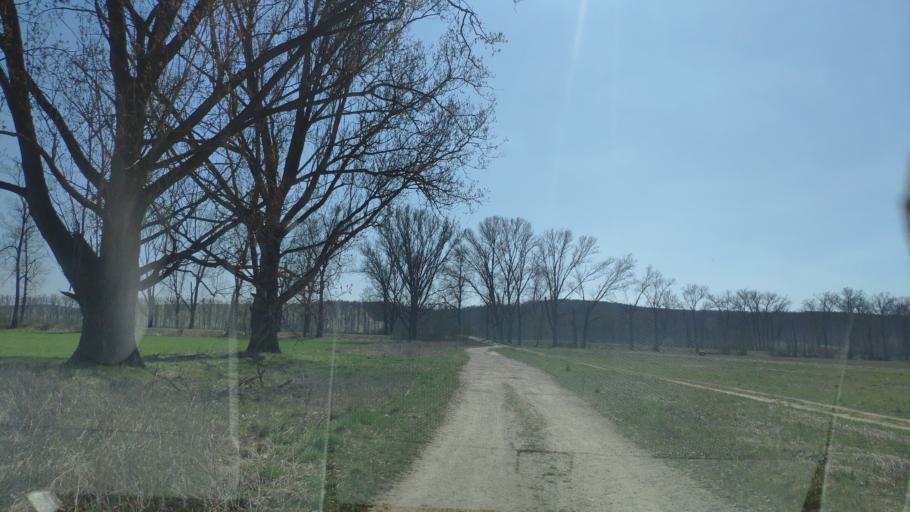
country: SK
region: Kosicky
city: Moldava nad Bodvou
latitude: 48.5740
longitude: 20.9472
